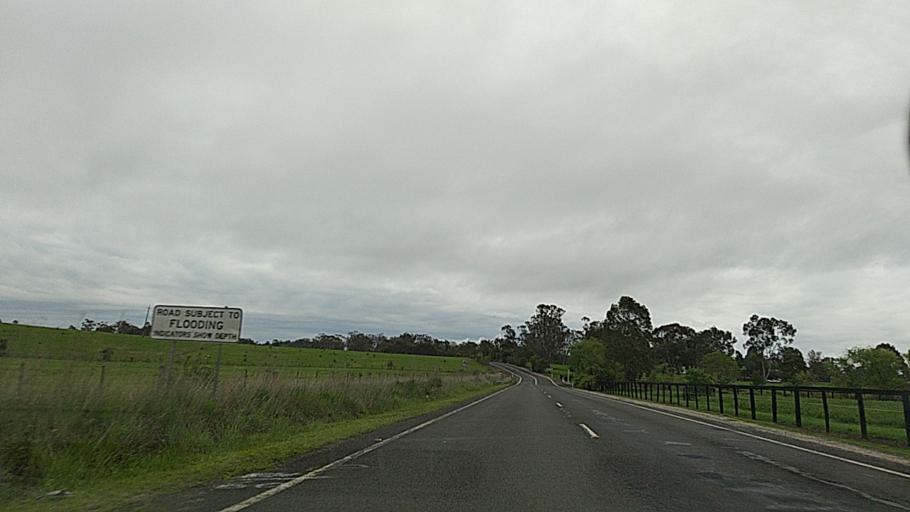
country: AU
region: New South Wales
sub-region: Wollondilly
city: Douglas Park
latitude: -34.1358
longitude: 150.7112
